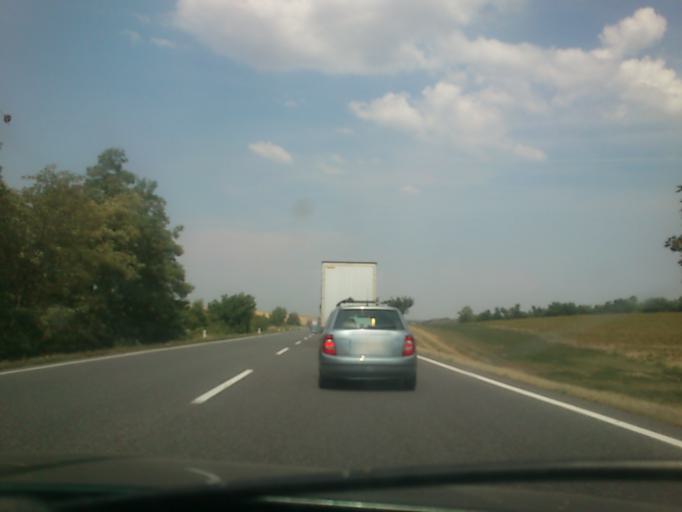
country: AT
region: Lower Austria
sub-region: Politischer Bezirk Mistelbach
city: Drasenhofen
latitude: 48.7251
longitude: 16.6571
